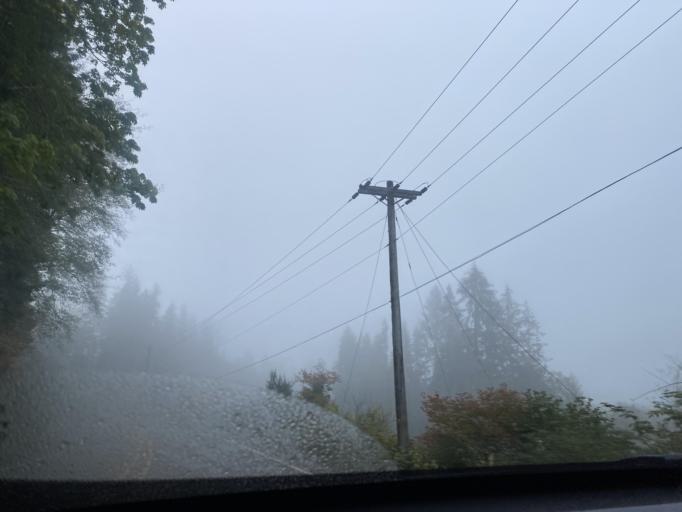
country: US
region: Washington
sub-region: Clallam County
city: Forks
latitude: 47.9290
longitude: -124.4098
